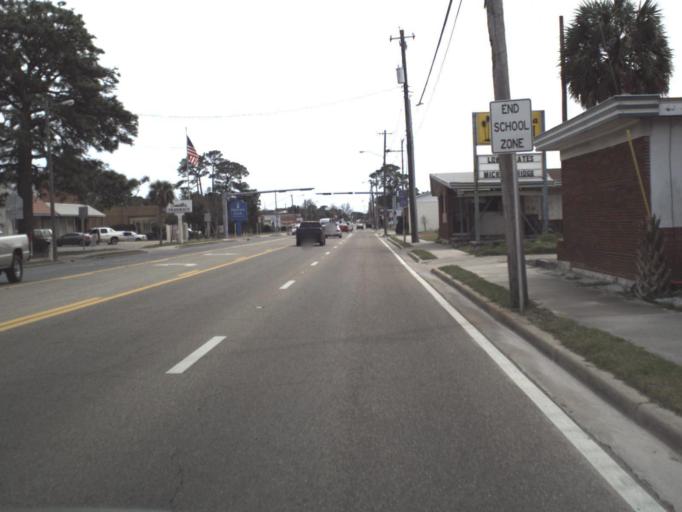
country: US
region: Florida
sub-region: Bay County
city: Panama City
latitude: 30.1692
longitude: -85.6603
